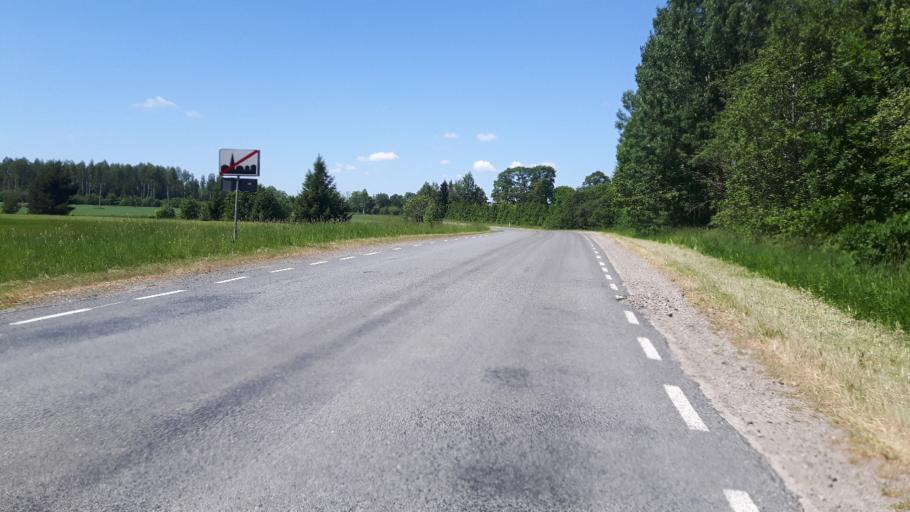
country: EE
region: Paernumaa
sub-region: Tootsi vald
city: Tootsi
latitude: 58.4937
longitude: 24.8928
